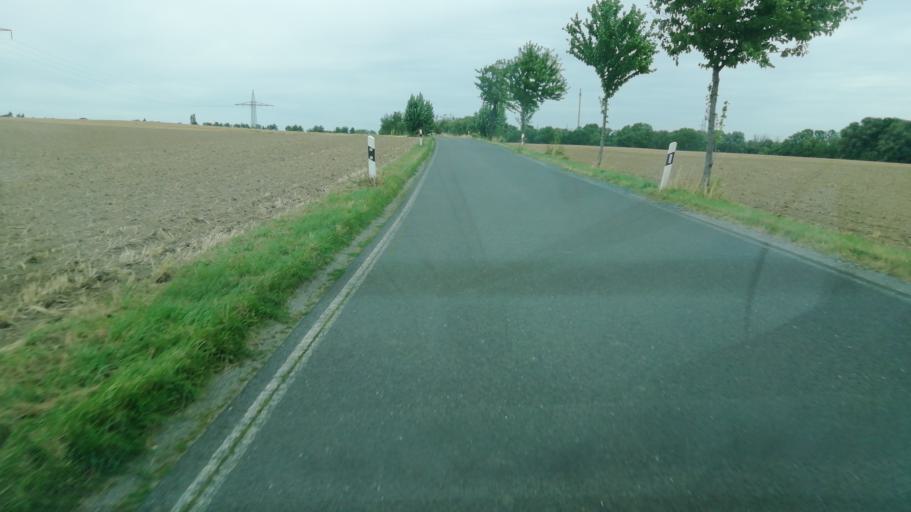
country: DE
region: Saxony
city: Wilsdruff
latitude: 51.0674
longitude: 13.5961
